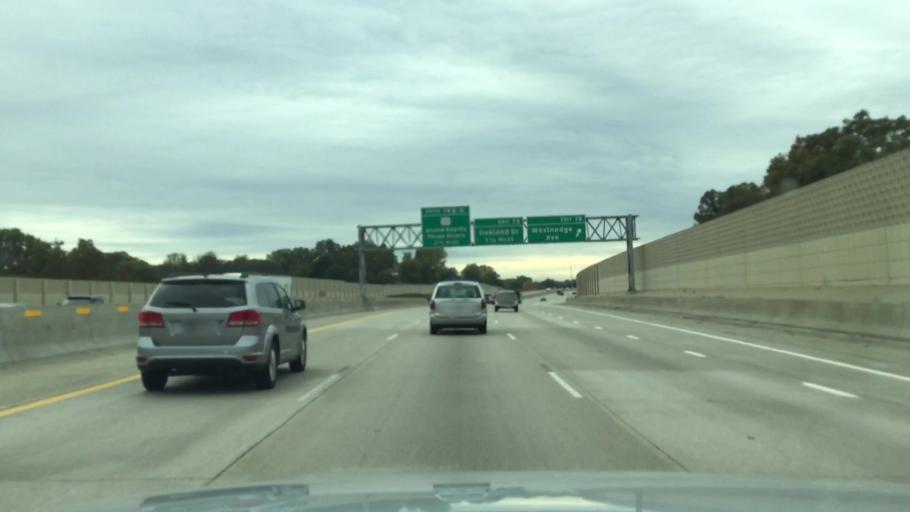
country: US
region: Michigan
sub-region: Kalamazoo County
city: Portage
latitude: 42.2373
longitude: -85.5805
